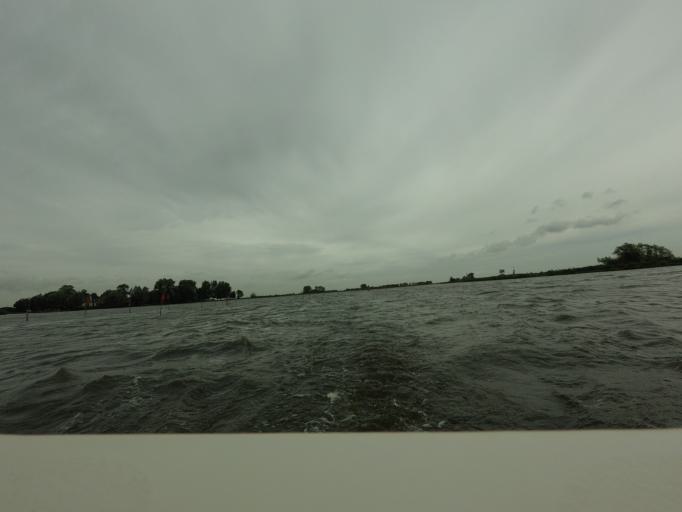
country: NL
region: Friesland
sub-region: Gemeente Boarnsterhim
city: Grou
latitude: 53.1062
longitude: 5.8560
